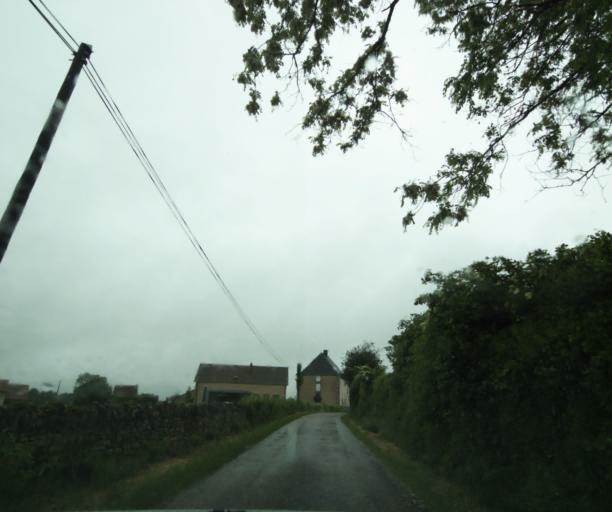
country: FR
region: Bourgogne
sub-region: Departement de Saone-et-Loire
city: Charolles
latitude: 46.4014
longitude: 4.2517
